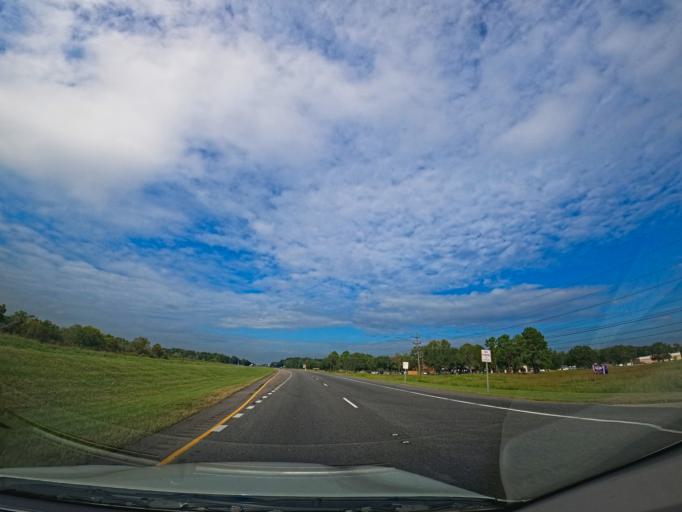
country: US
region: Louisiana
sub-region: Saint Mary Parish
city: Patterson
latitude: 29.6897
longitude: -91.3102
